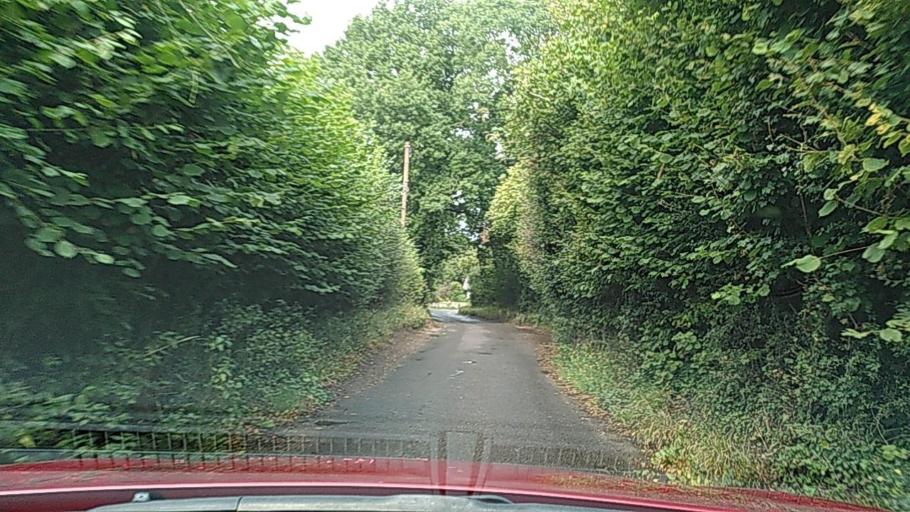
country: GB
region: England
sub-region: Oxfordshire
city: Henley on Thames
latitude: 51.5165
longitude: -0.9244
